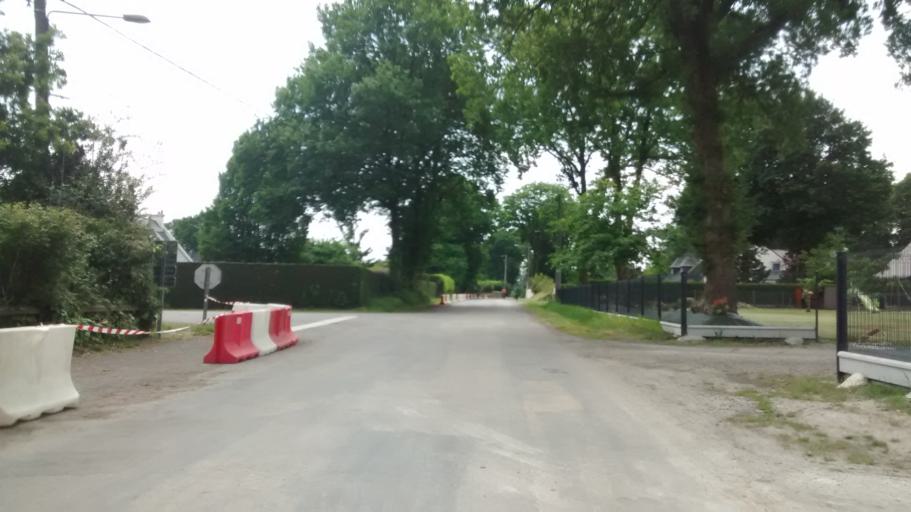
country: FR
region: Brittany
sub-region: Departement du Morbihan
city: Questembert
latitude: 47.6876
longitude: -2.4453
